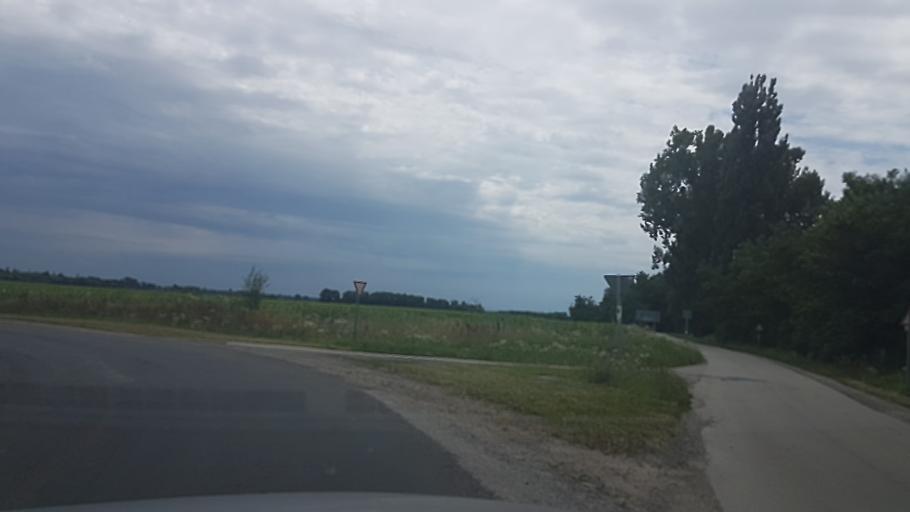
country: HU
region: Somogy
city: Barcs
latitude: 45.9602
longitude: 17.5885
